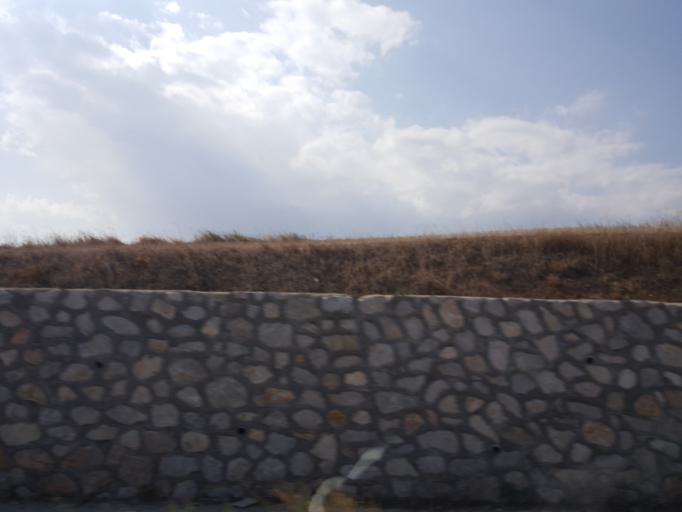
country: TR
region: Corum
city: Alaca
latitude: 40.1493
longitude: 34.8837
